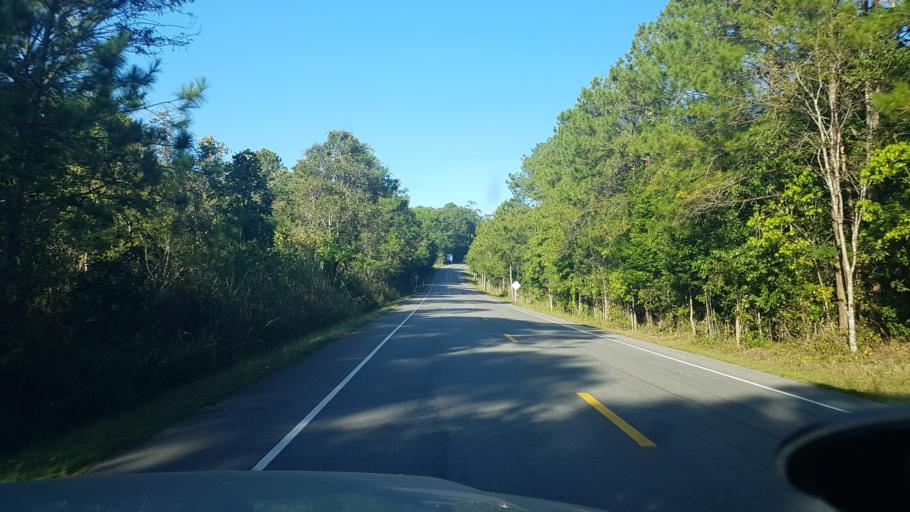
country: TH
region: Phetchabun
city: Nam Nao
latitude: 16.7301
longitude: 101.5591
